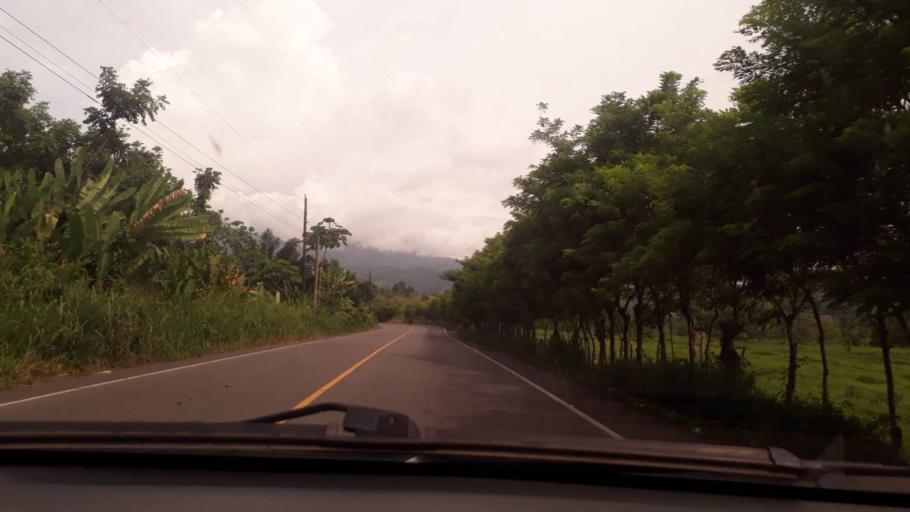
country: HN
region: Cortes
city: Potrerillos
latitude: 15.6000
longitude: -88.3825
